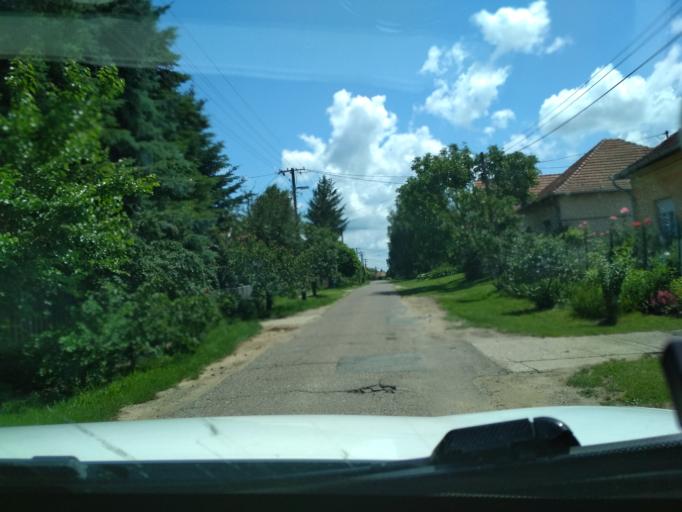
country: HU
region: Jasz-Nagykun-Szolnok
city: Tiszafured
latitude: 47.6059
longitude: 20.7537
